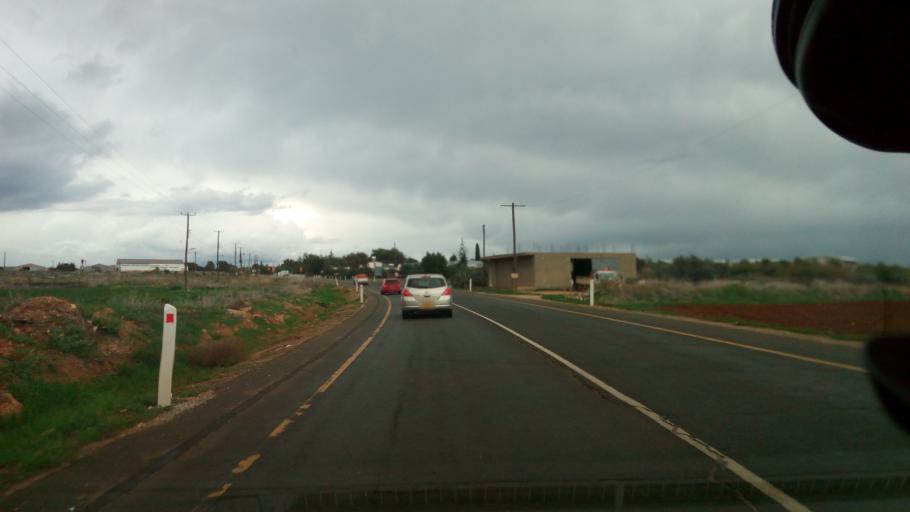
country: CY
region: Ammochostos
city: Frenaros
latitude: 35.0276
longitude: 33.9117
